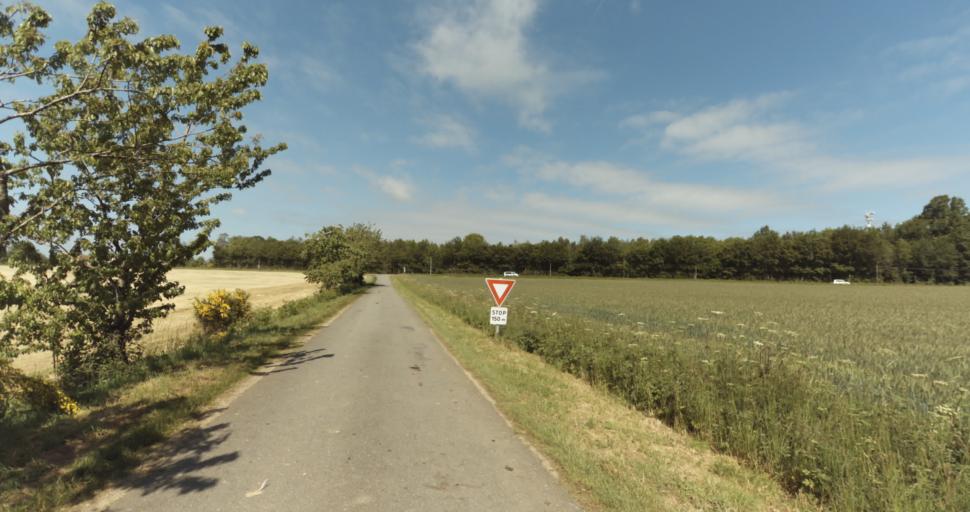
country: FR
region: Limousin
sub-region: Departement de la Haute-Vienne
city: Solignac
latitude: 45.7216
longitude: 1.2564
